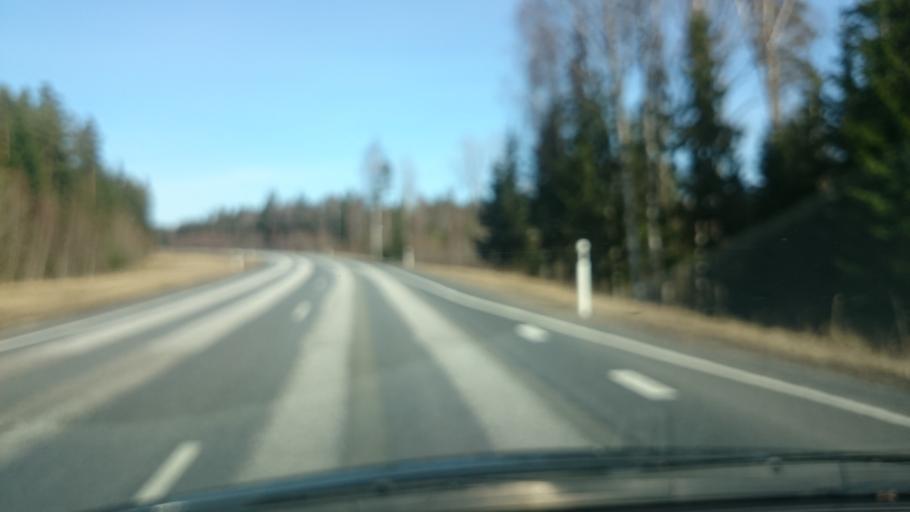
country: EE
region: Jaervamaa
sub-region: Tueri vald
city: Sarevere
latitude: 58.7354
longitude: 25.2982
